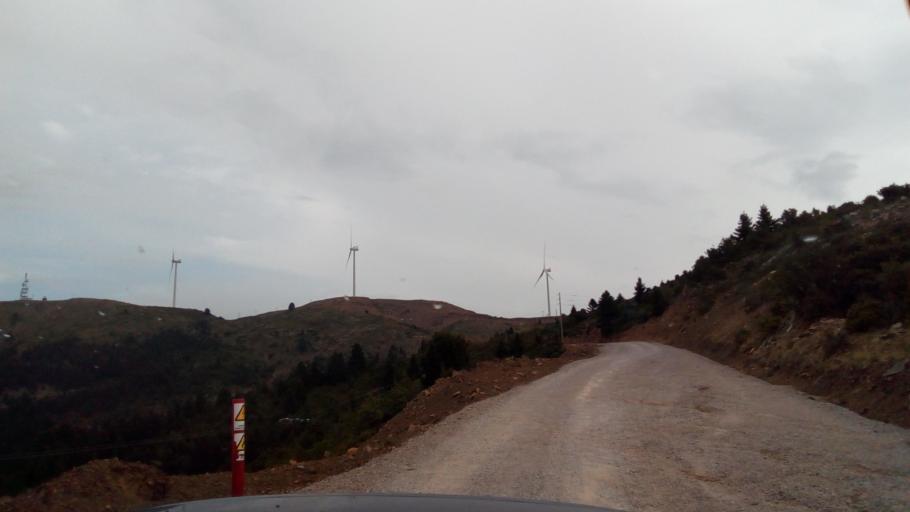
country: GR
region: Central Greece
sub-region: Nomos Fokidos
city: Lidoriki
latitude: 38.4473
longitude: 22.0729
